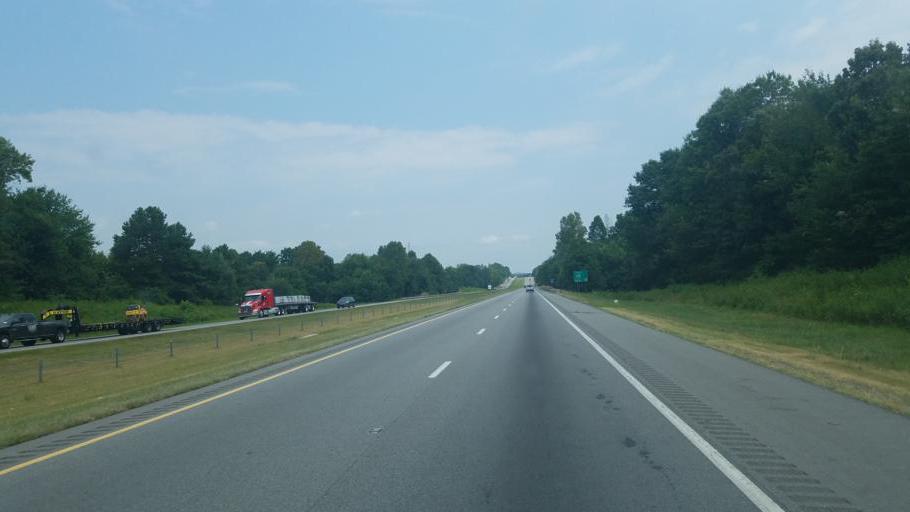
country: US
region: North Carolina
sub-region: Yadkin County
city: Yadkinville
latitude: 36.0552
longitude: -80.8225
